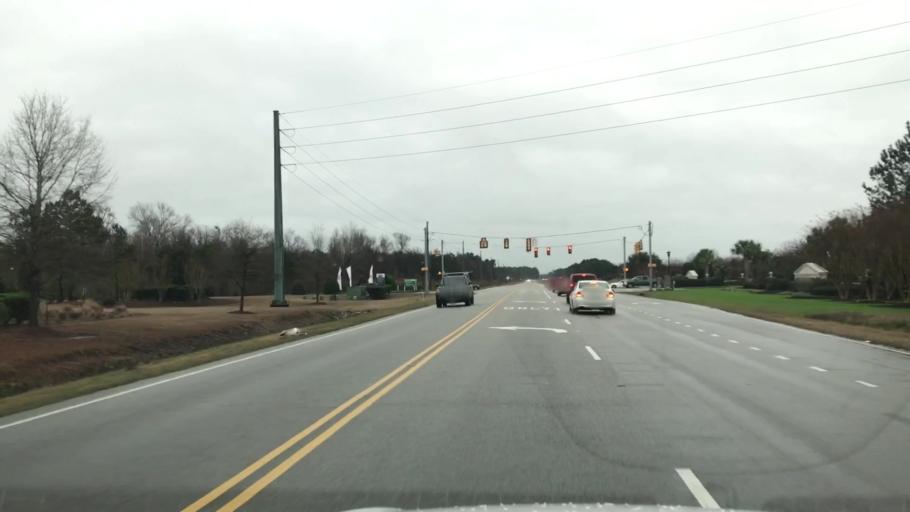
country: US
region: South Carolina
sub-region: Horry County
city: Myrtle Beach
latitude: 33.7362
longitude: -78.8979
